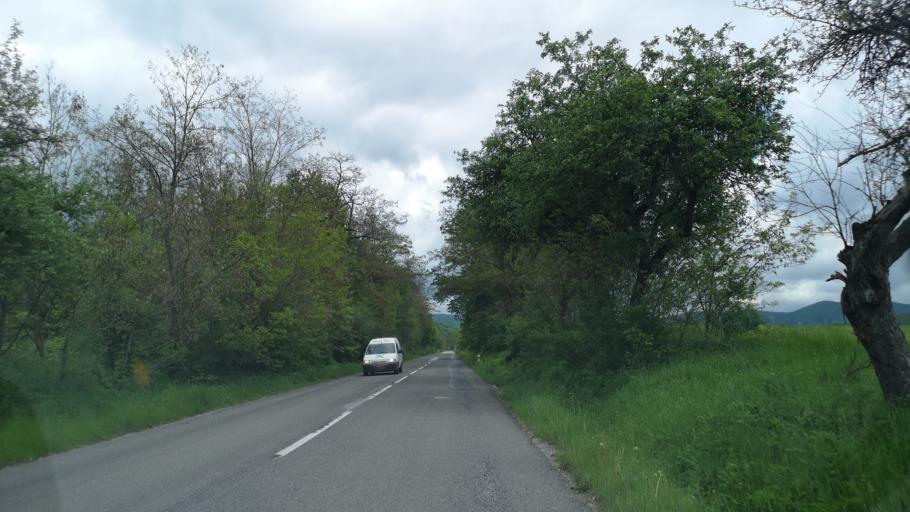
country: SK
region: Kosicky
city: Dobsina
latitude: 48.6357
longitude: 20.3371
